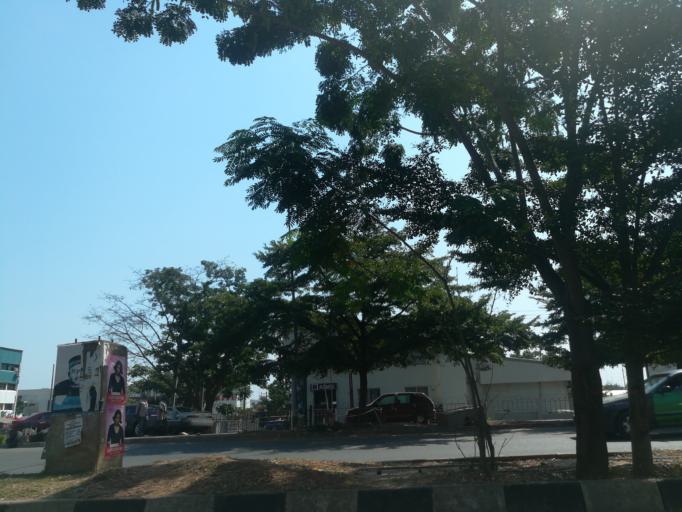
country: NG
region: Abuja Federal Capital Territory
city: Abuja
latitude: 9.0640
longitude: 7.4564
